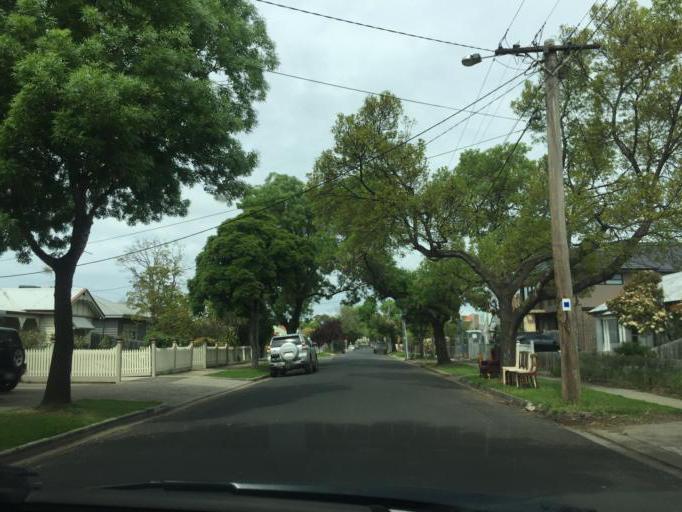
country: AU
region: Victoria
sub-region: Hobsons Bay
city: South Kingsville
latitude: -37.8271
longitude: 144.8765
